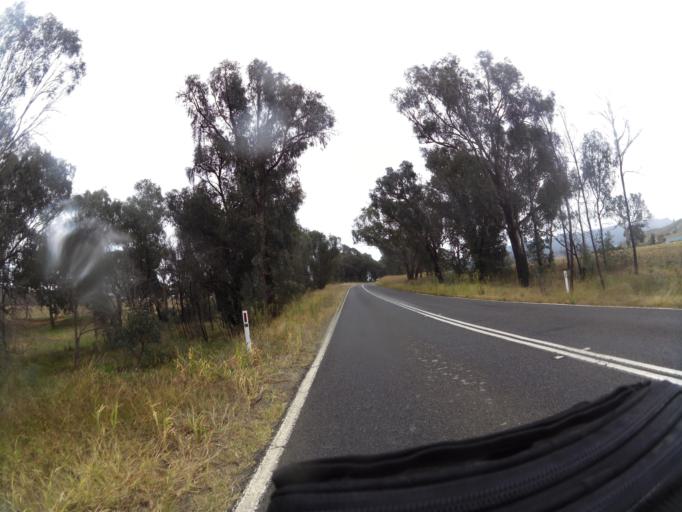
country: AU
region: New South Wales
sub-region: Greater Hume Shire
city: Holbrook
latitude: -36.2079
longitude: 147.8018
